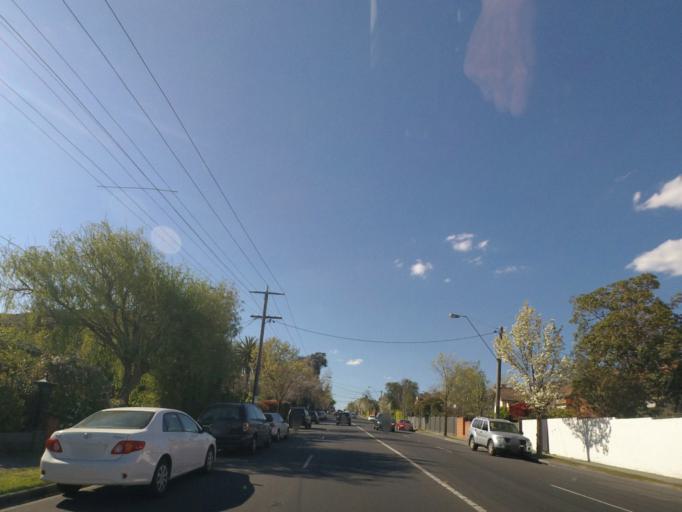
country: AU
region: Victoria
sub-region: Boroondara
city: Kew
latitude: -37.8184
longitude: 145.0269
